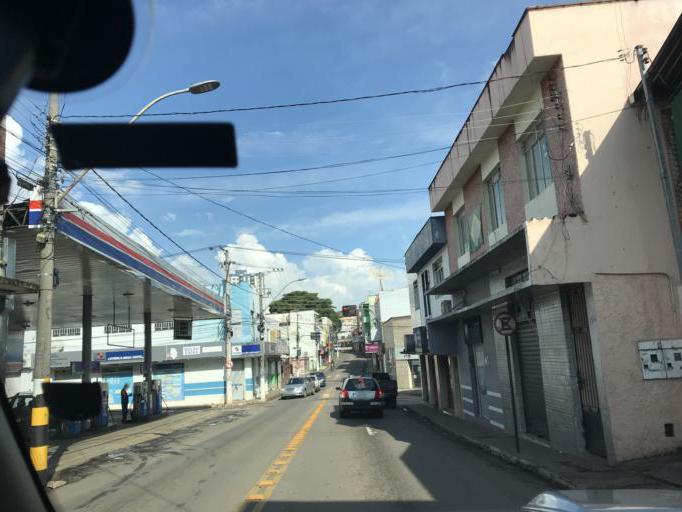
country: BR
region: Minas Gerais
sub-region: Tres Coracoes
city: Tres Coracoes
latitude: -21.6939
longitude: -45.2584
